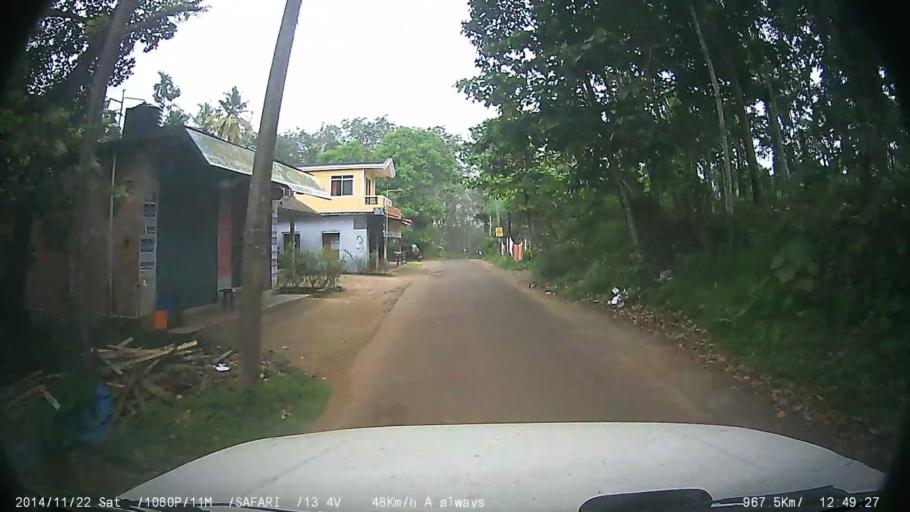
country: IN
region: Kerala
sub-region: Ernakulam
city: Piravam
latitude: 9.7928
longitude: 76.5471
